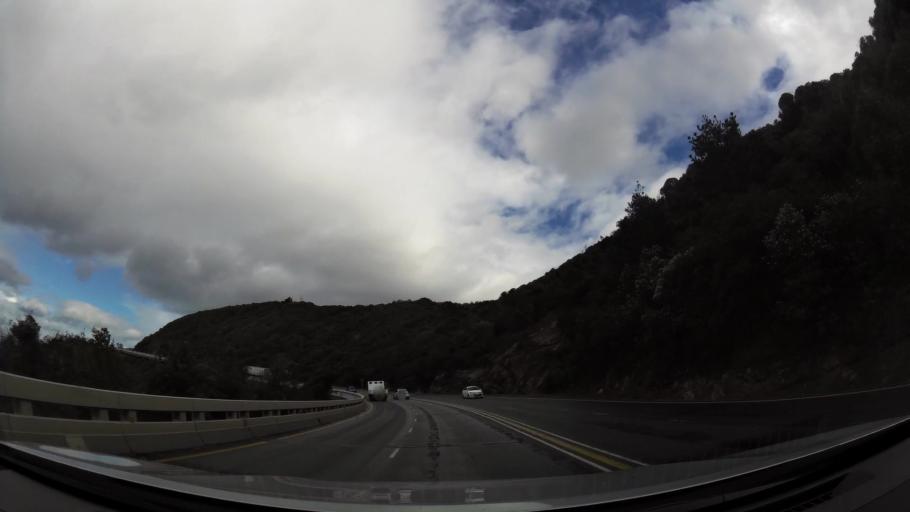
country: ZA
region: Western Cape
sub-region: Eden District Municipality
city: George
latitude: -33.9950
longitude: 22.5640
